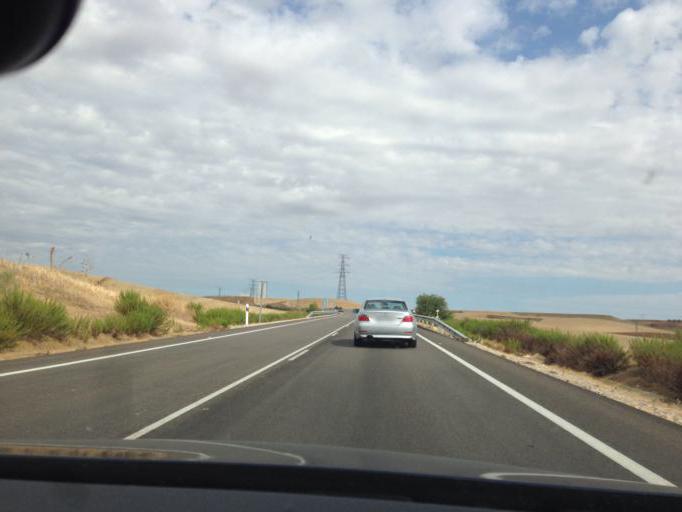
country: ES
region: Madrid
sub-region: Provincia de Madrid
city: Ajalvir
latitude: 40.5455
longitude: -3.4735
